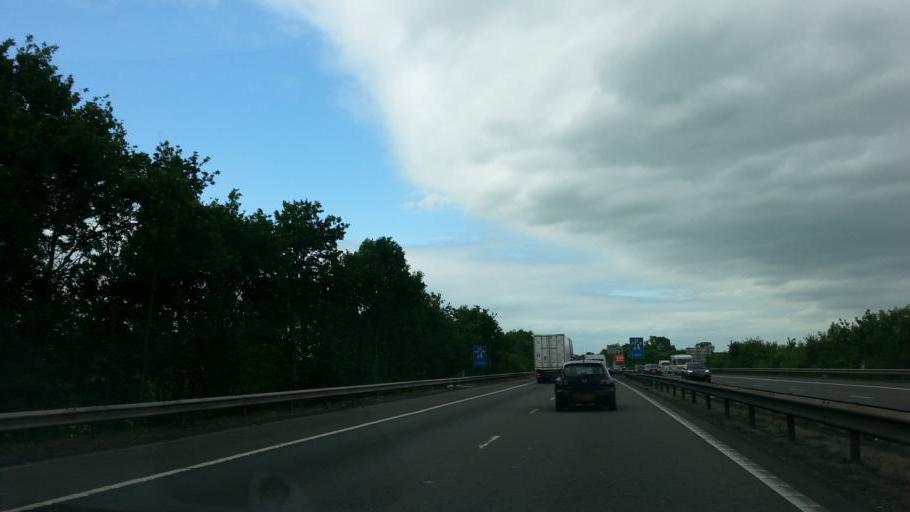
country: GB
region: England
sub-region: Derbyshire
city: Netherseal
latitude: 52.6776
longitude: -1.5553
